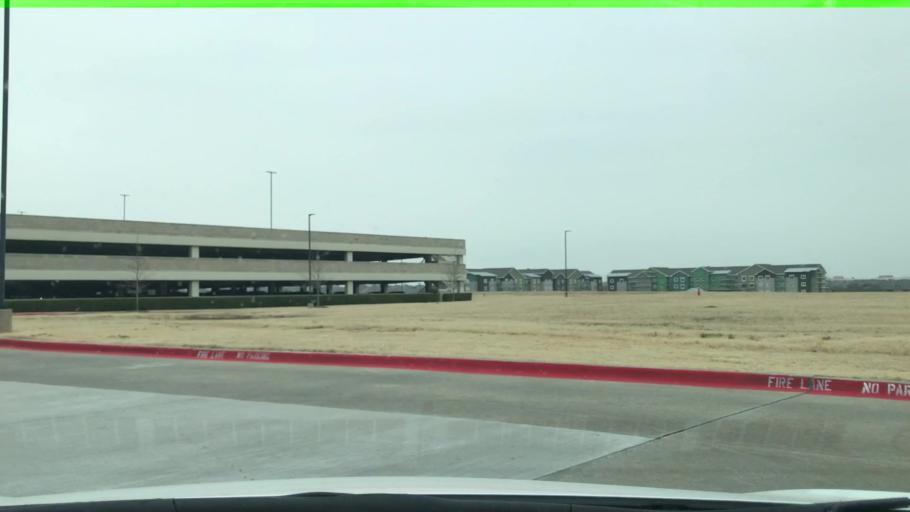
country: US
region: Texas
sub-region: Dallas County
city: Coppell
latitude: 32.8976
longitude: -96.9715
